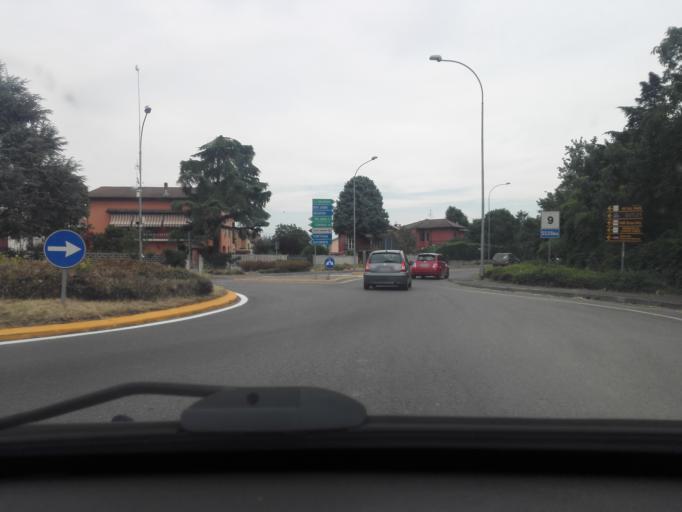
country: IT
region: Piedmont
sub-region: Provincia di Alessandria
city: Pozzolo Formigaro
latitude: 44.7892
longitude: 8.7860
